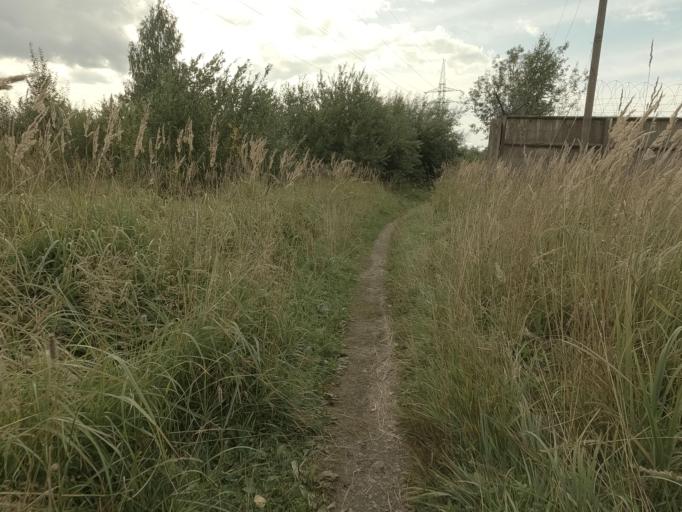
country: RU
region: Leningrad
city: Kirovsk
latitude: 59.8690
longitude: 30.9913
